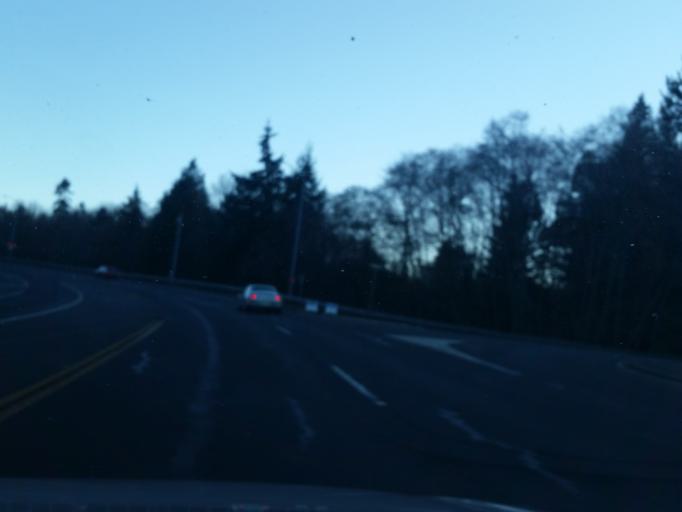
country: US
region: Washington
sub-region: Snohomish County
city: Woodway
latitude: 47.8037
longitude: -122.3833
